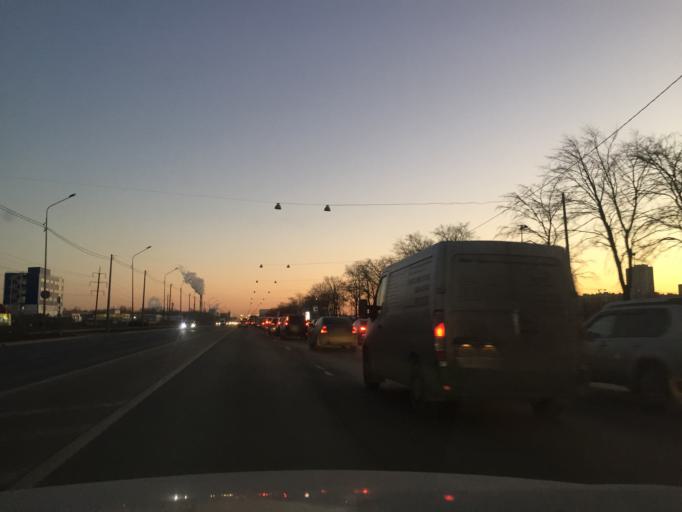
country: RU
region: St.-Petersburg
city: Obukhovo
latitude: 59.8577
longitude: 30.4217
